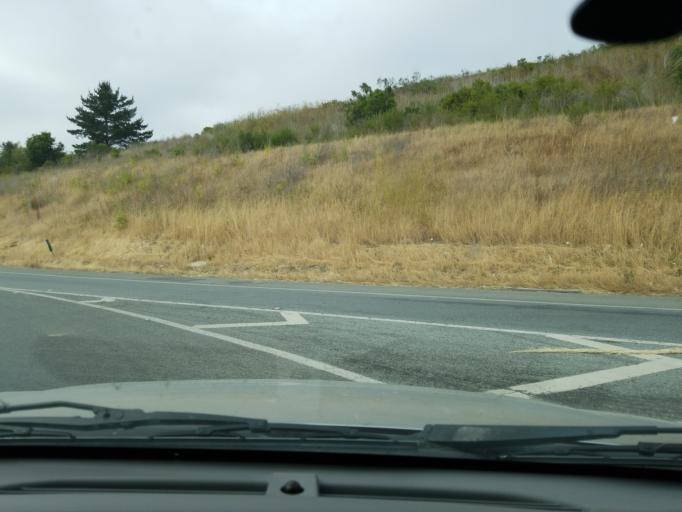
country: US
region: California
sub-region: Monterey County
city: Las Lomas
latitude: 36.8686
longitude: -121.7437
